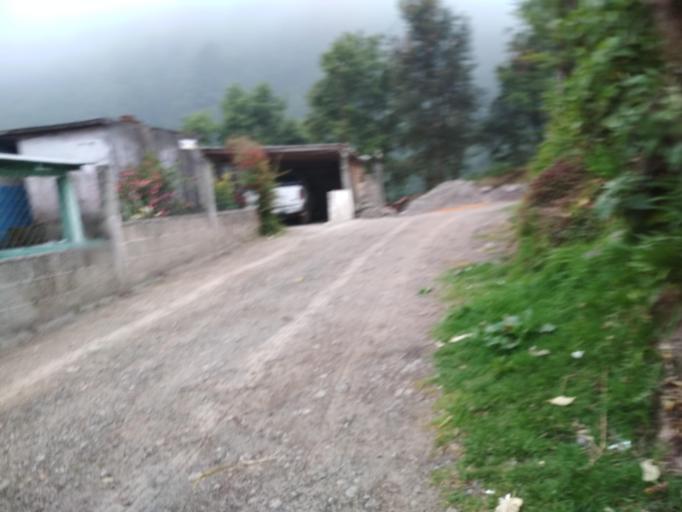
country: MX
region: Veracruz
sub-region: Mariano Escobedo
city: San Isidro el Berro
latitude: 18.9517
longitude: -97.1847
